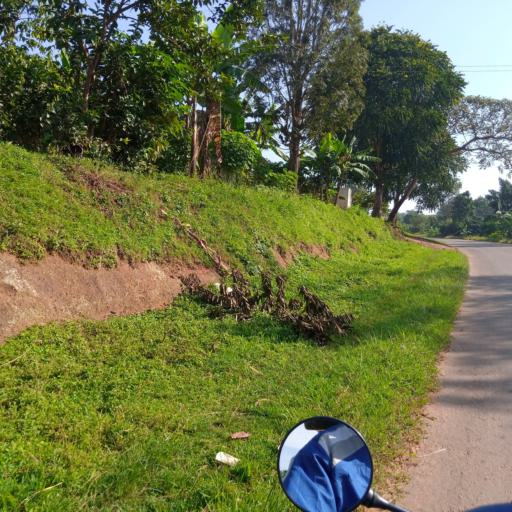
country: UG
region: Central Region
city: Masaka
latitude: -0.4499
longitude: 31.6685
